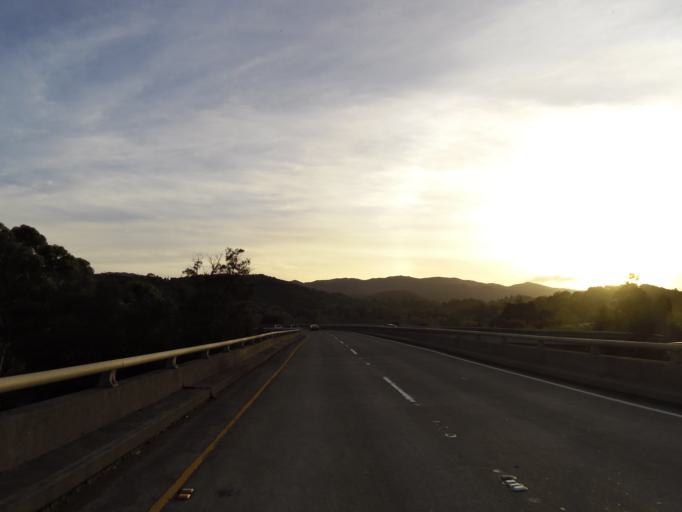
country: US
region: California
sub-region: Marin County
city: Novato
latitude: 38.0813
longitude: -122.5445
